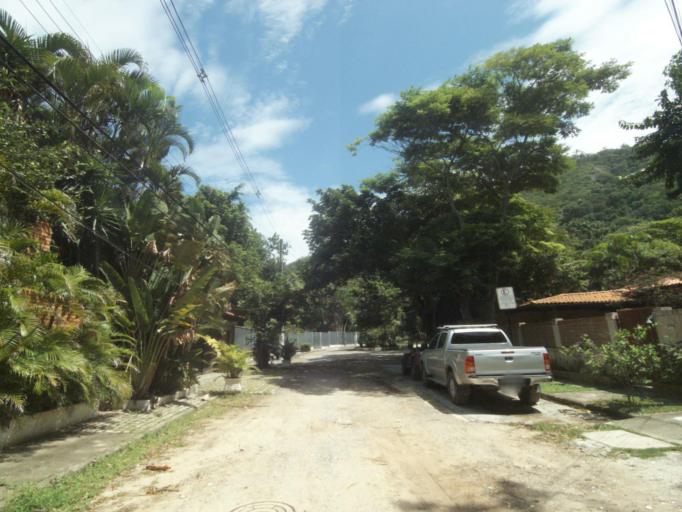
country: BR
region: Rio de Janeiro
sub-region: Niteroi
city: Niteroi
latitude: -22.9718
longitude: -43.0345
